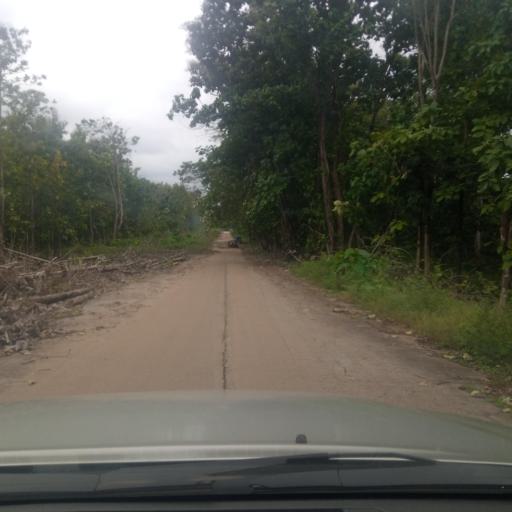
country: NG
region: Ebonyi
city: Effium
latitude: 6.6216
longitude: 8.0457
